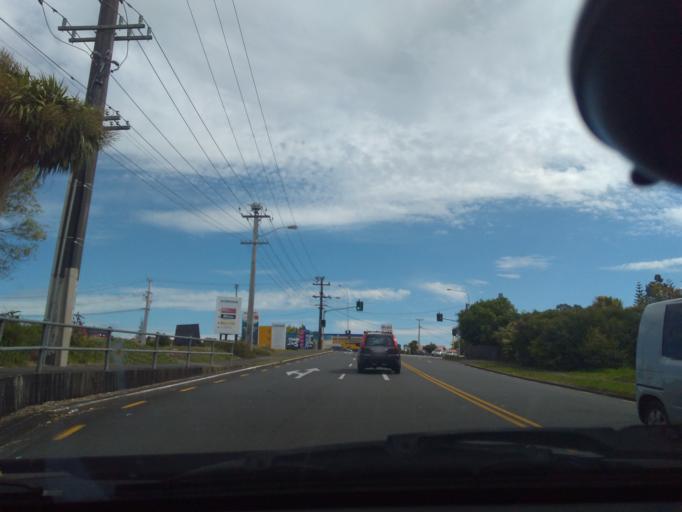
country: NZ
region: Auckland
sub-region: Auckland
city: Waitakere
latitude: -36.9112
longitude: 174.6759
